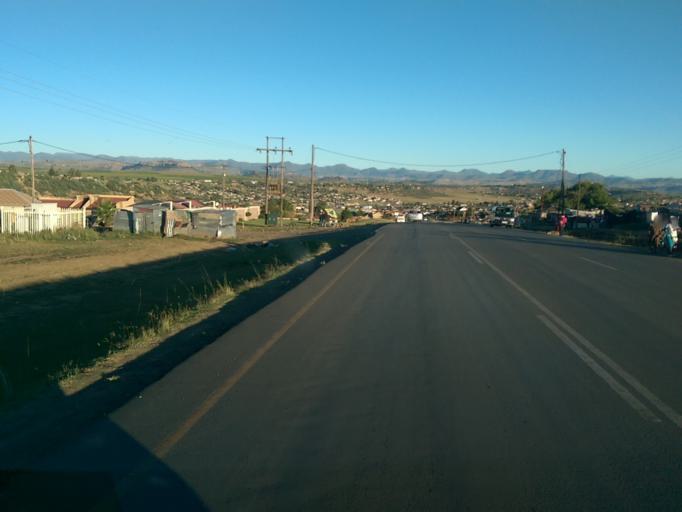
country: LS
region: Maseru
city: Maseru
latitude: -29.3719
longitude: 27.5432
